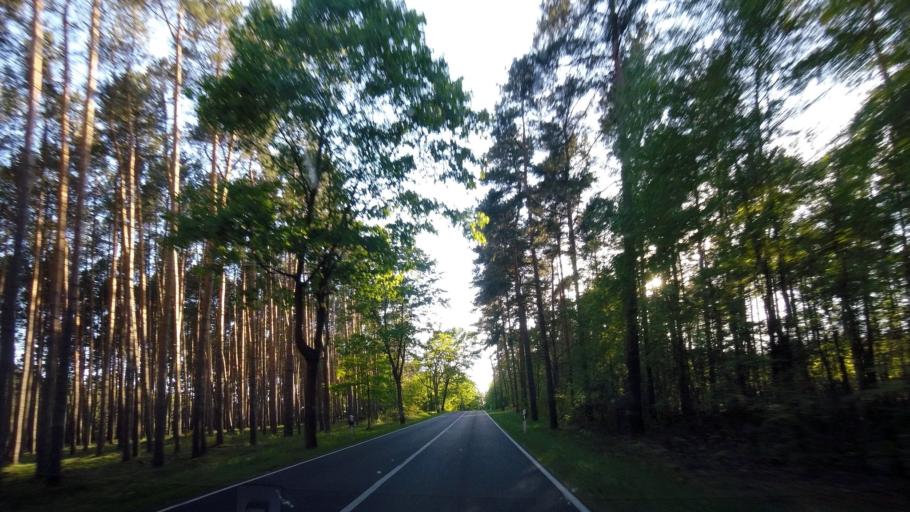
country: DE
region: Brandenburg
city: Luckenwalde
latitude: 51.9894
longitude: 13.2301
